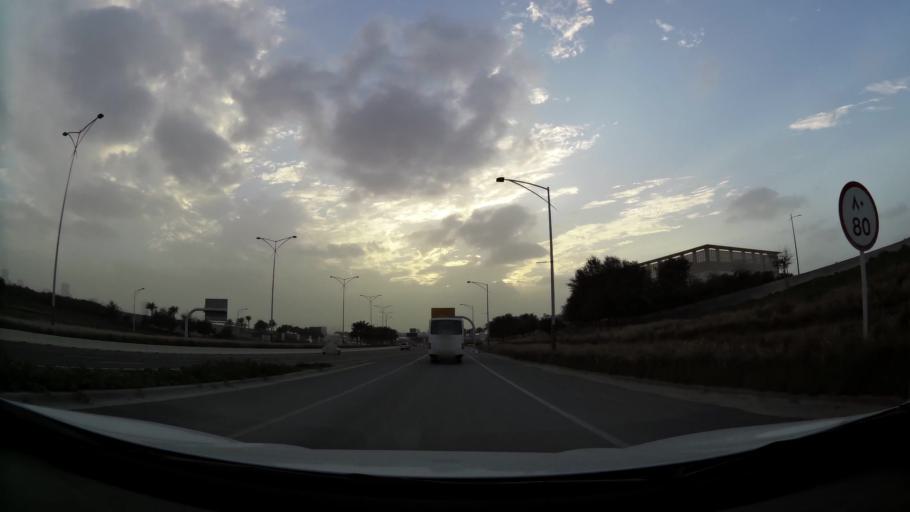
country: AE
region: Abu Dhabi
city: Abu Dhabi
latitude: 24.5310
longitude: 54.4162
